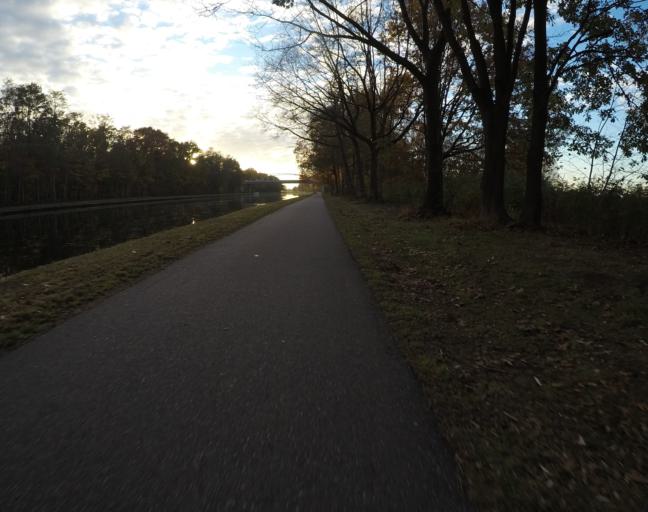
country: BE
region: Flanders
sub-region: Provincie Antwerpen
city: Geel
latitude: 51.2002
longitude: 4.9745
